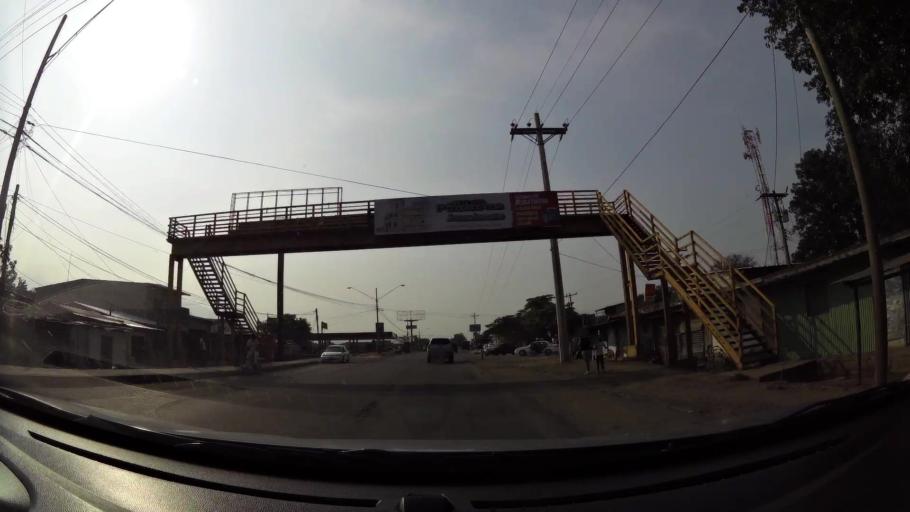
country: HN
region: Comayagua
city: Comayagua
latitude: 14.4502
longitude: -87.6440
